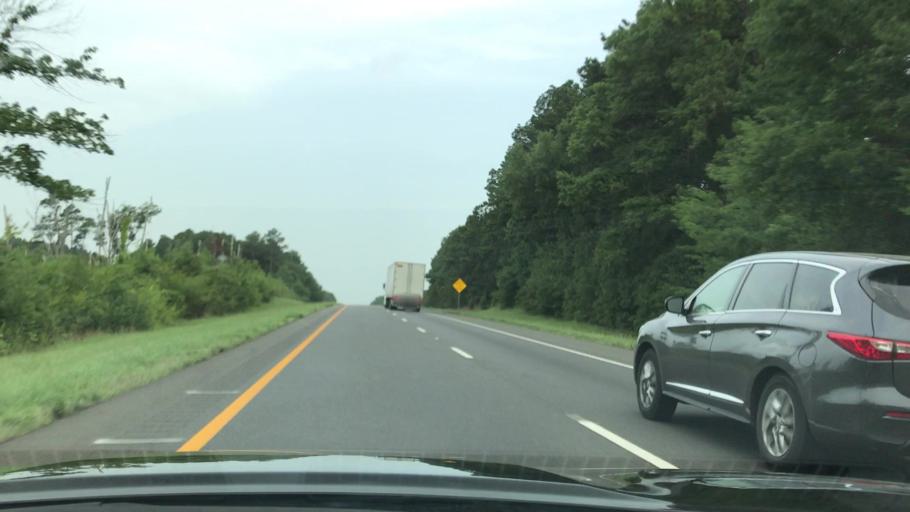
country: US
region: Texas
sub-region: Harrison County
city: Marshall
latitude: 32.4901
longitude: -94.3852
